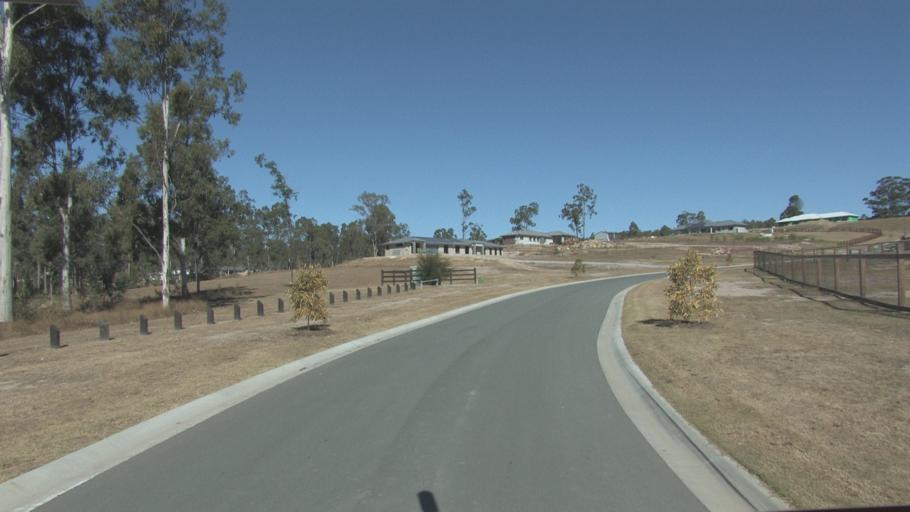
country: AU
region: Queensland
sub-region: Logan
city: Cedar Vale
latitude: -27.8722
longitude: 153.0431
